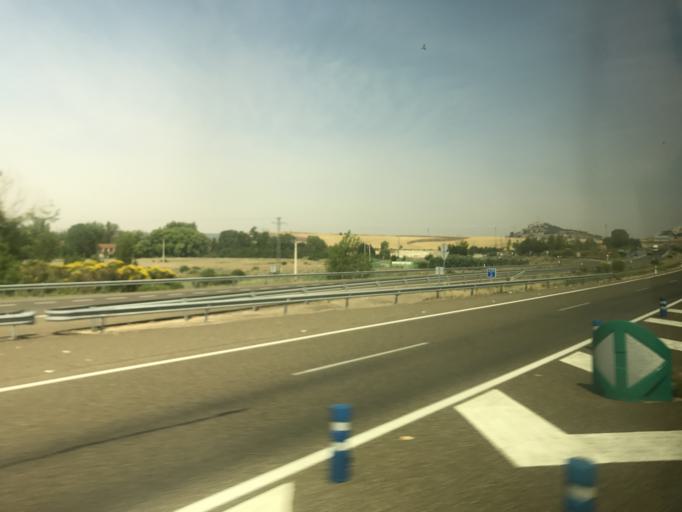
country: ES
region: Castille and Leon
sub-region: Provincia de Palencia
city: Villalobon
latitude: 42.0177
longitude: -4.5064
